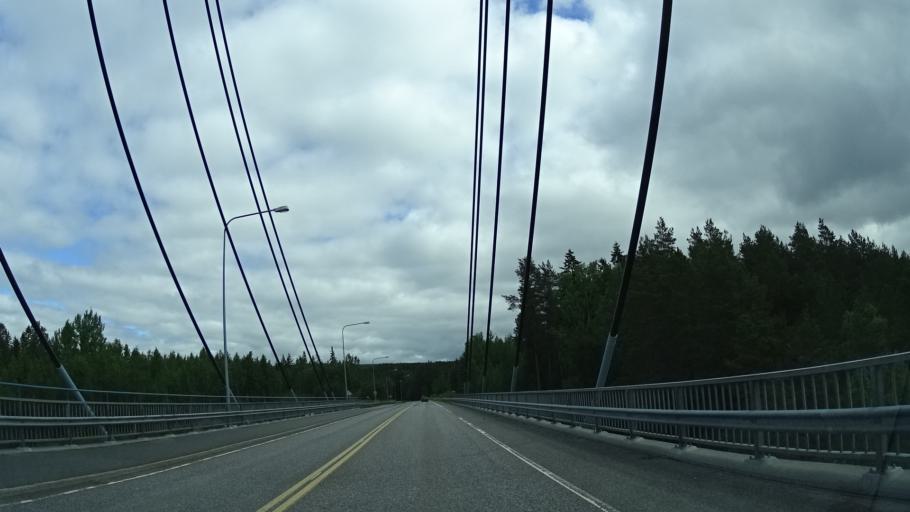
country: FI
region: Central Finland
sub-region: Jyvaeskylae
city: Korpilahti
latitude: 61.9997
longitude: 25.6776
